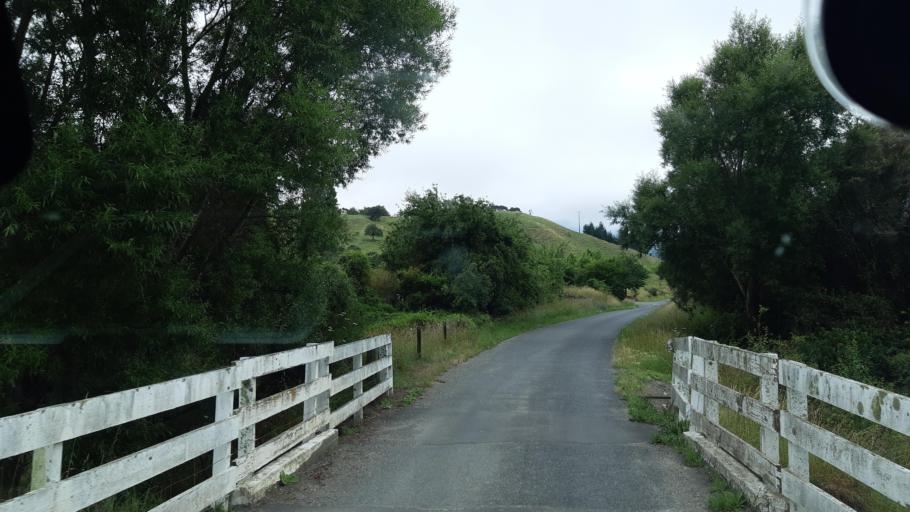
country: NZ
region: Marlborough
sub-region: Marlborough District
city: Blenheim
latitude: -41.9896
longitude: 173.9983
